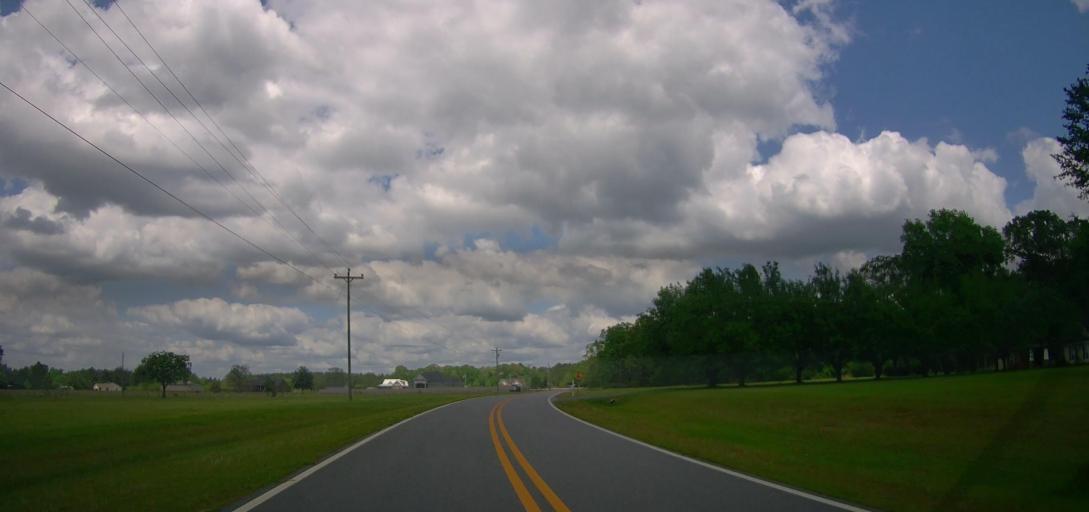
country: US
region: Georgia
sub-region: Laurens County
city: Dublin
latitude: 32.6004
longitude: -82.9369
